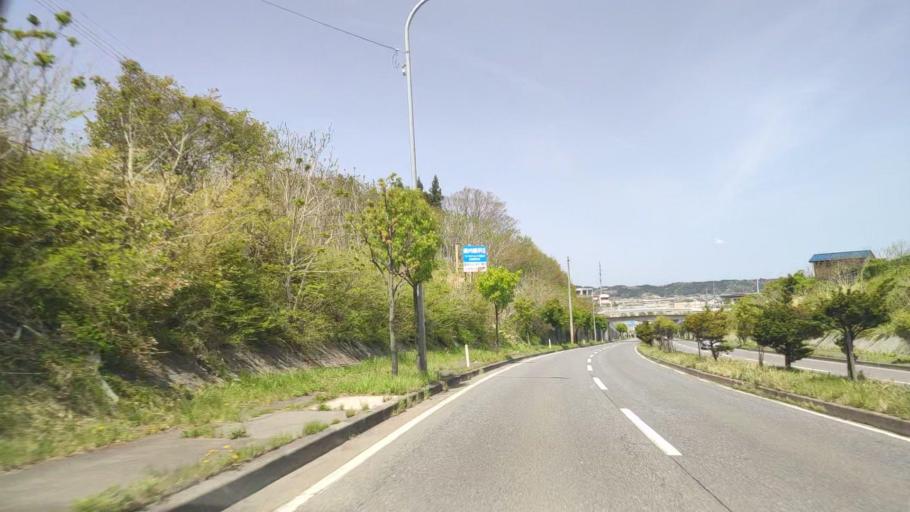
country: JP
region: Aomori
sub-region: Hachinohe Shi
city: Uchimaru
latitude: 40.4973
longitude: 141.4578
